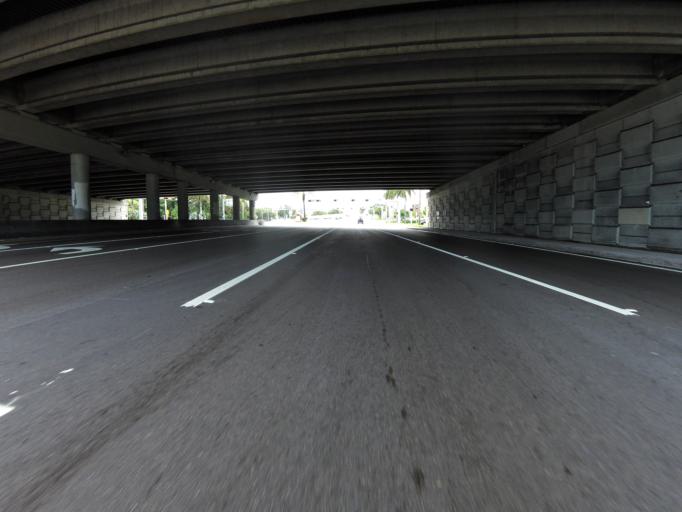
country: US
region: Florida
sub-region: Broward County
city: Hollywood
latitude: 26.0334
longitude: -80.1639
